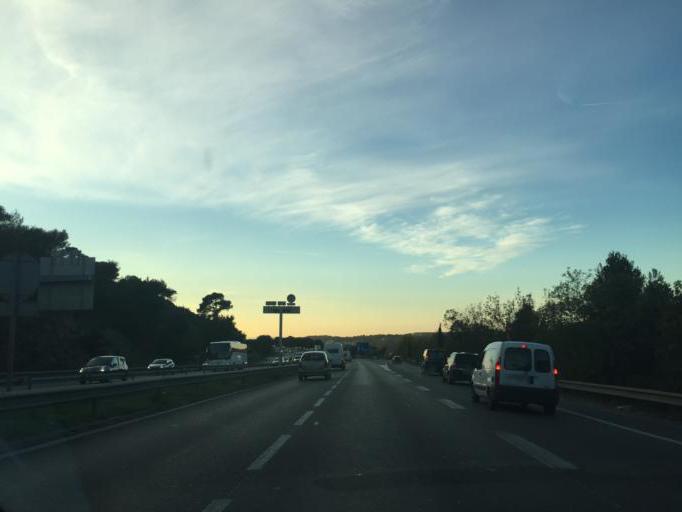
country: FR
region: Provence-Alpes-Cote d'Azur
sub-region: Departement des Bouches-du-Rhone
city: Les Pennes-Mirabeau
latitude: 43.4053
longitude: 5.3389
